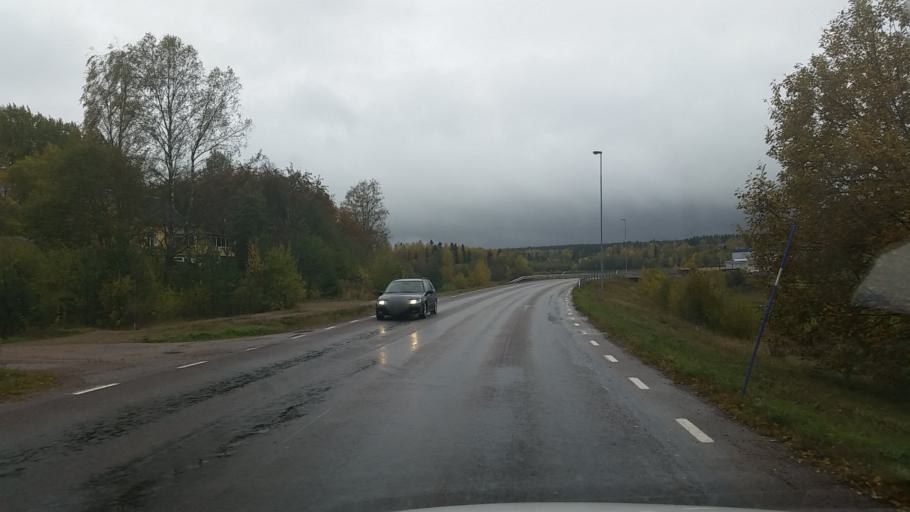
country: SE
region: Gaevleborg
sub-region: Sandvikens Kommun
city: Jarbo
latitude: 60.5724
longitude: 16.5348
